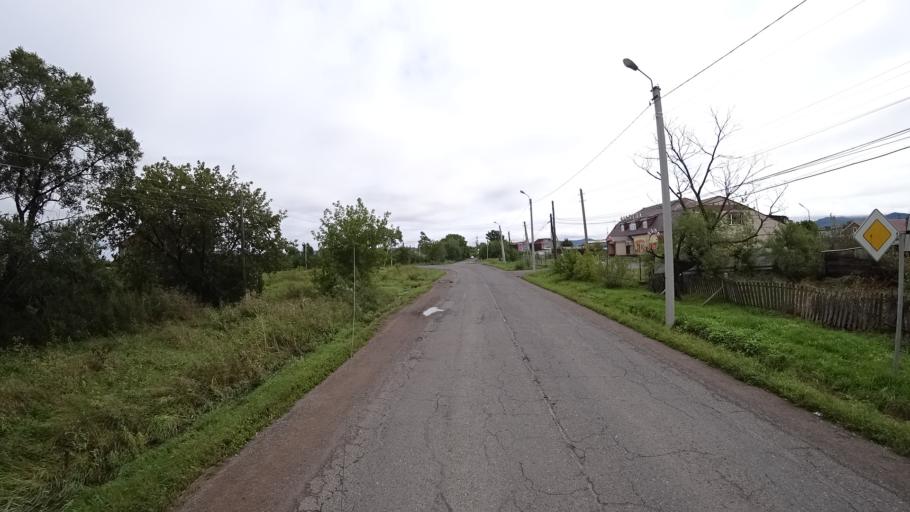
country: RU
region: Primorskiy
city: Monastyrishche
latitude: 44.1986
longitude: 132.4619
